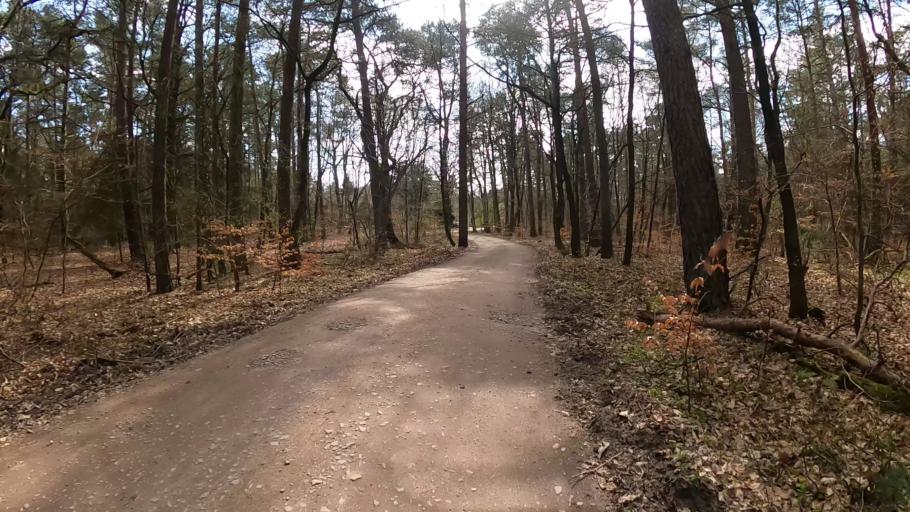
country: DE
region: Lower Saxony
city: Neu Wulmstorf
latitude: 53.4401
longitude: 9.8510
